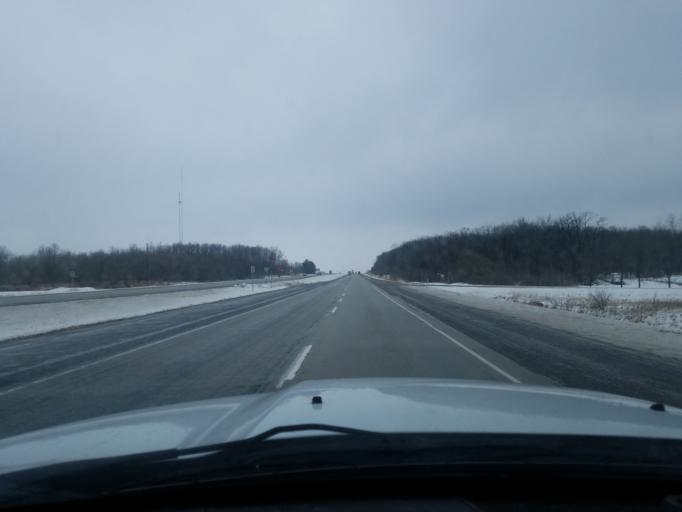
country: US
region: Indiana
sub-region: Fulton County
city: Rochester
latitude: 41.1099
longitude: -86.2397
